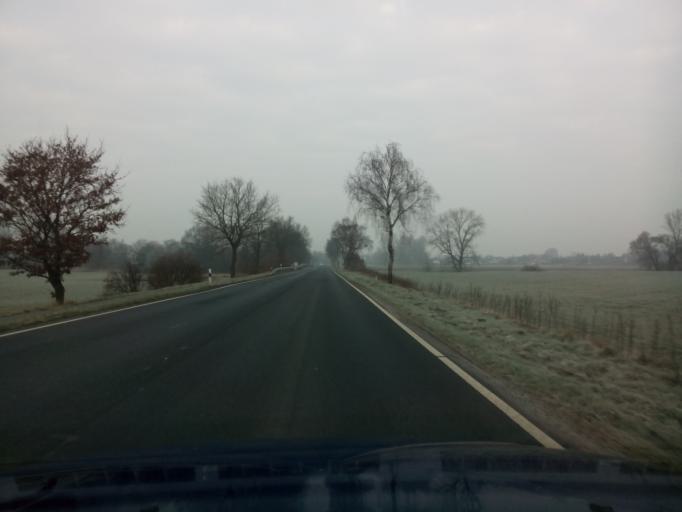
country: DE
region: Lower Saxony
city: Loxstedt
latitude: 53.4491
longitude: 8.6123
